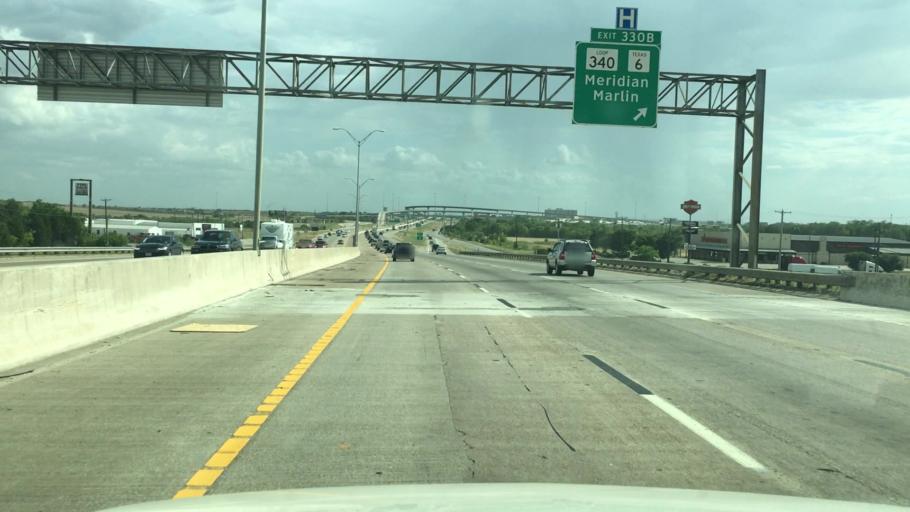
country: US
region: Texas
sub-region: McLennan County
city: Beverly
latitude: 31.5081
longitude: -97.1431
